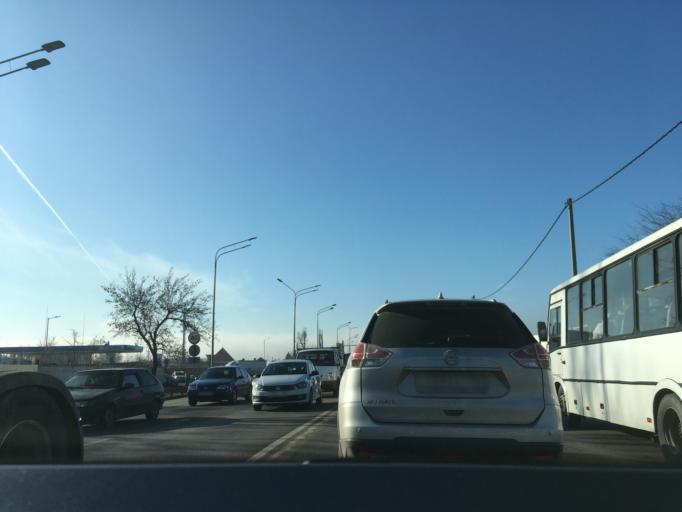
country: RU
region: Krasnodarskiy
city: Krasnodar
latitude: 45.1283
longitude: 39.0142
